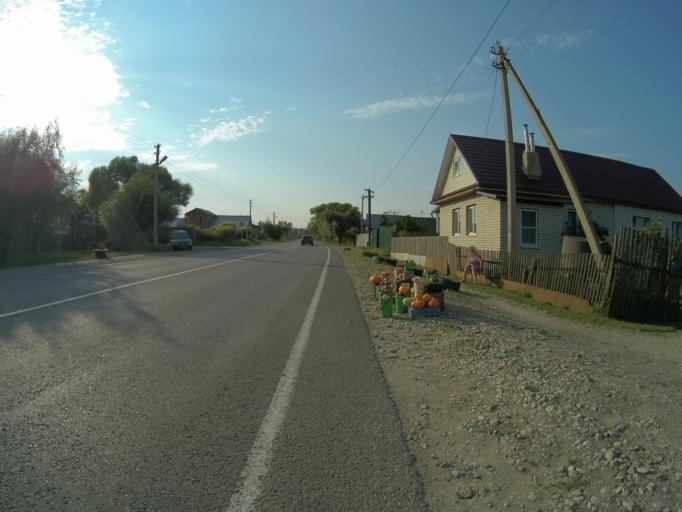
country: RU
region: Vladimir
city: Kommunar
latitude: 56.0429
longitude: 40.5442
